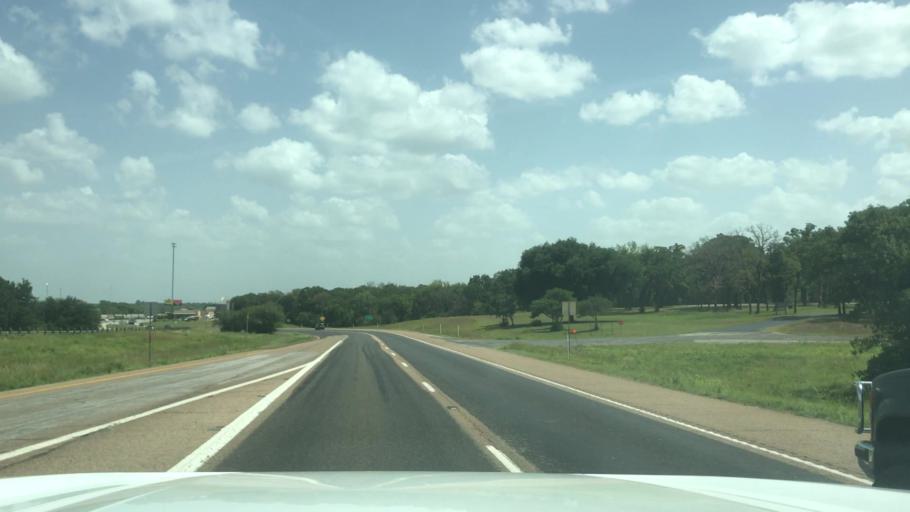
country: US
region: Texas
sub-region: Robertson County
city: Hearne
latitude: 30.9043
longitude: -96.6084
